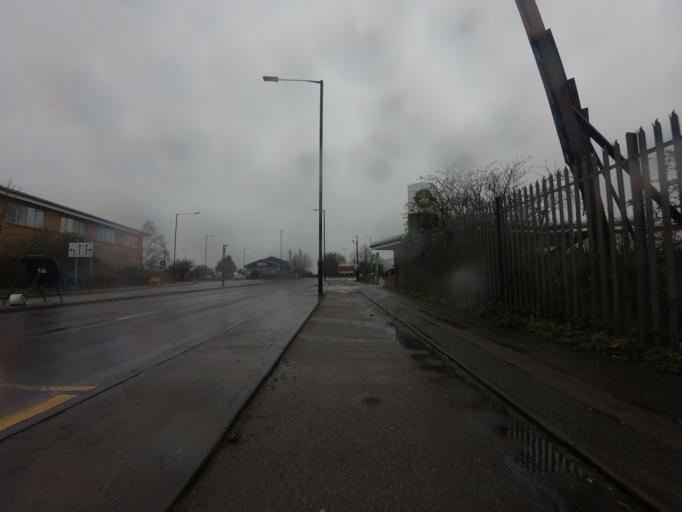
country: GB
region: England
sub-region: Hertfordshire
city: Waltham Cross
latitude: 51.6479
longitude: -0.0302
